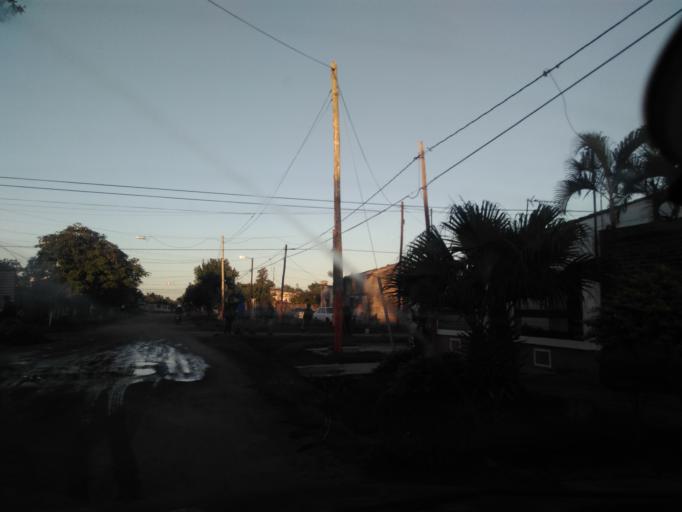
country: AR
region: Chaco
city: Resistencia
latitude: -27.4661
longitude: -58.9963
